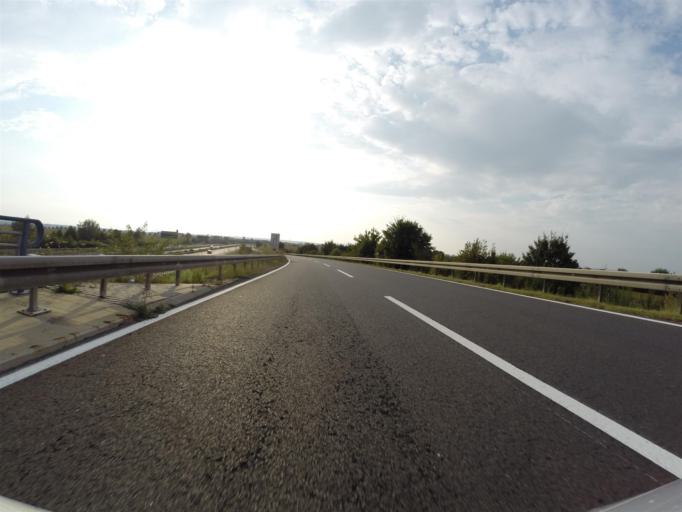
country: DE
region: Saxony-Anhalt
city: Grosskorbetha
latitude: 51.2376
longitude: 12.0532
